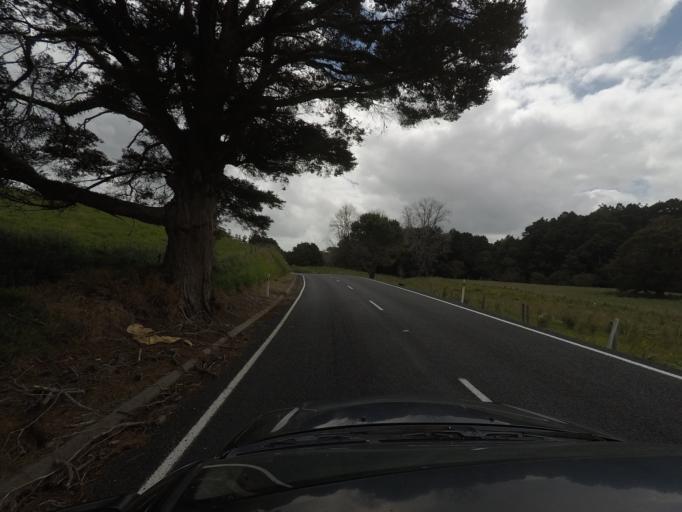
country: NZ
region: Auckland
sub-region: Auckland
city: Parakai
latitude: -36.5029
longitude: 174.5184
